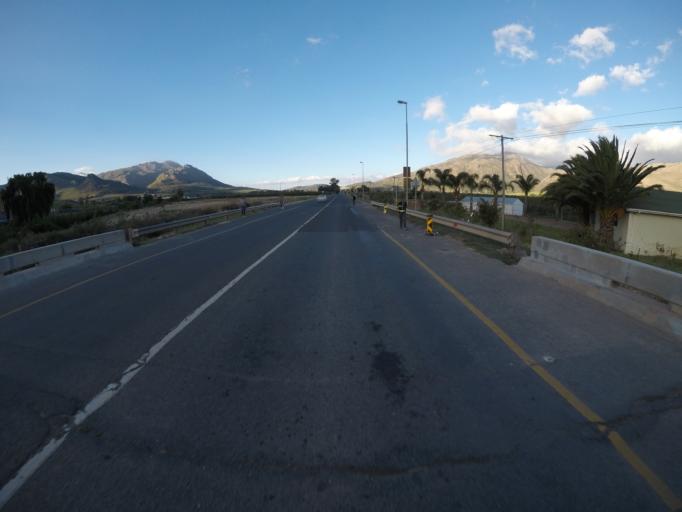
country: ZA
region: Western Cape
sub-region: Overberg District Municipality
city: Caledon
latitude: -33.9857
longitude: 19.2971
